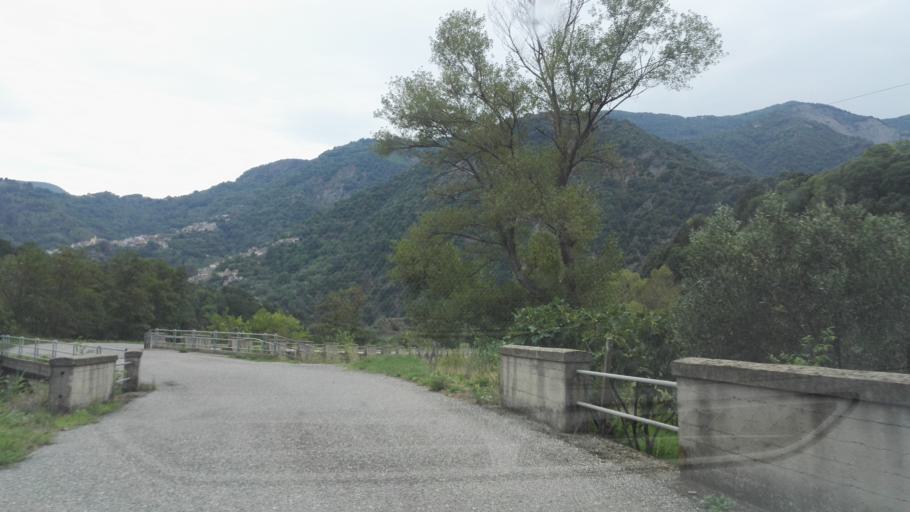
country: IT
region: Calabria
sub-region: Provincia di Reggio Calabria
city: Caulonia
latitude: 38.4229
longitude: 16.3826
